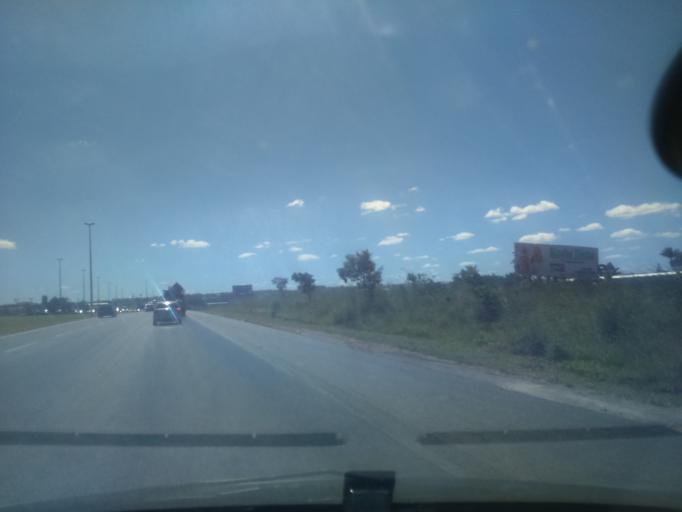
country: BR
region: Goias
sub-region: Luziania
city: Luziania
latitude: -16.1146
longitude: -47.9683
